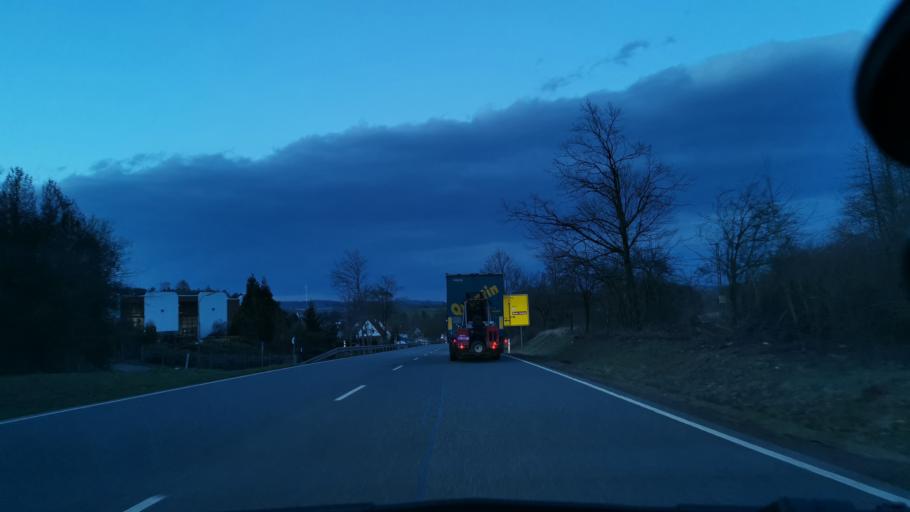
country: DE
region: Hesse
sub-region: Regierungsbezirk Kassel
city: Cornberg
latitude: 51.0371
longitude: 9.8604
